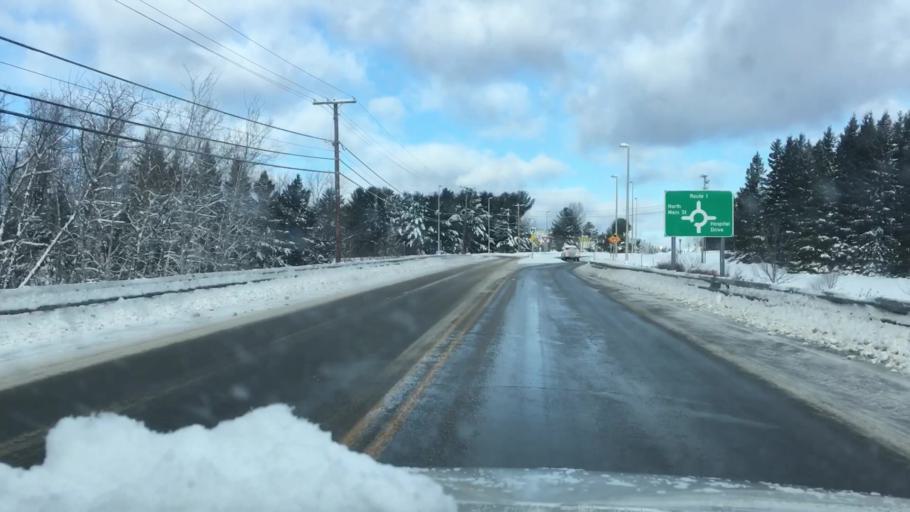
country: US
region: Maine
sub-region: Aroostook County
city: Caribou
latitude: 46.8776
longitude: -68.0089
